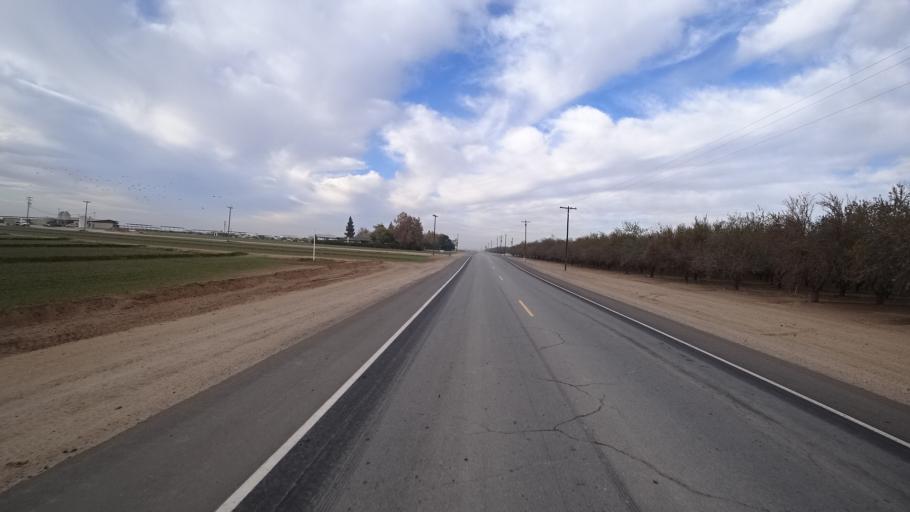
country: US
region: California
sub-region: Kern County
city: Rosedale
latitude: 35.4197
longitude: -119.2005
